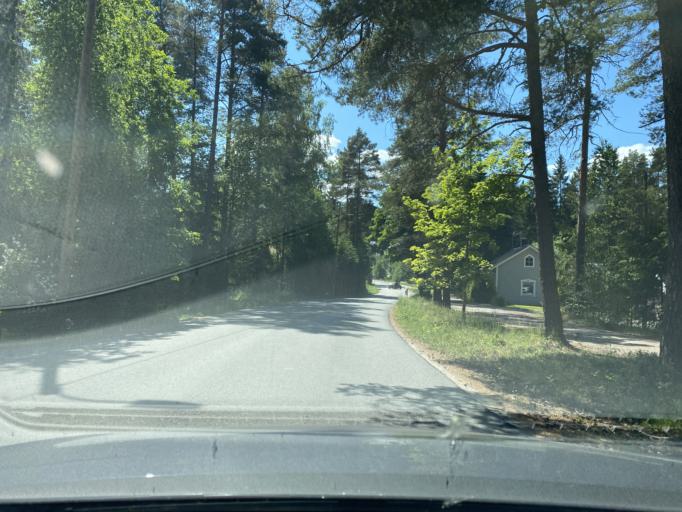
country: FI
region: Satakunta
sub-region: Rauma
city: Eura
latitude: 61.1300
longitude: 22.1659
